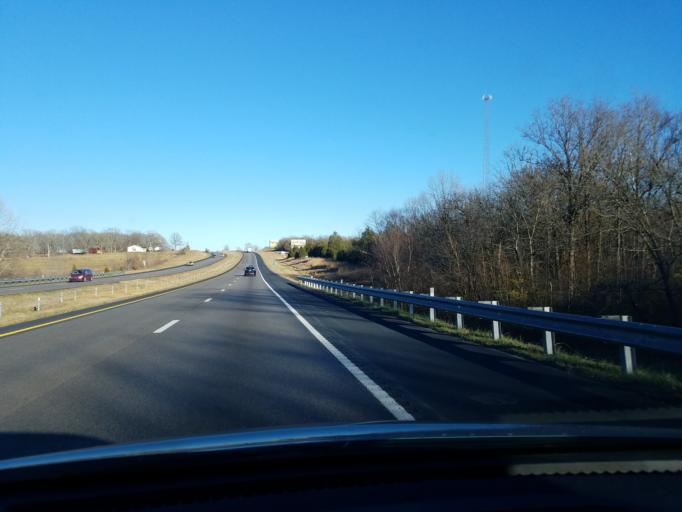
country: US
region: Missouri
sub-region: Phelps County
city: Saint James
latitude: 38.0139
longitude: -91.5894
